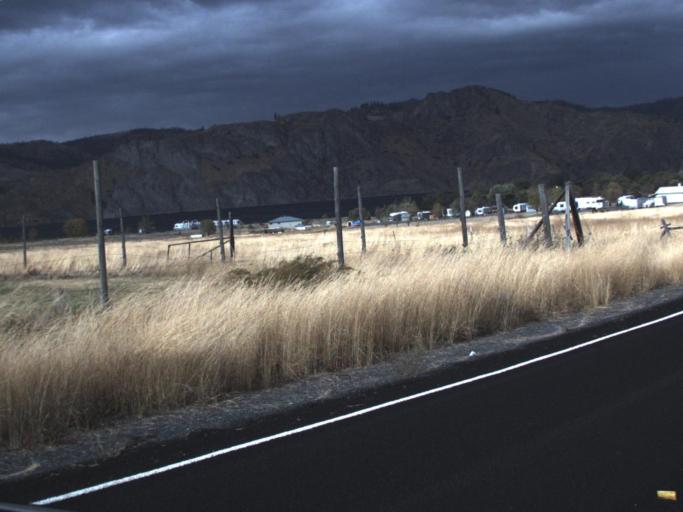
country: US
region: Washington
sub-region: Okanogan County
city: Coulee Dam
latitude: 47.9215
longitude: -118.6895
